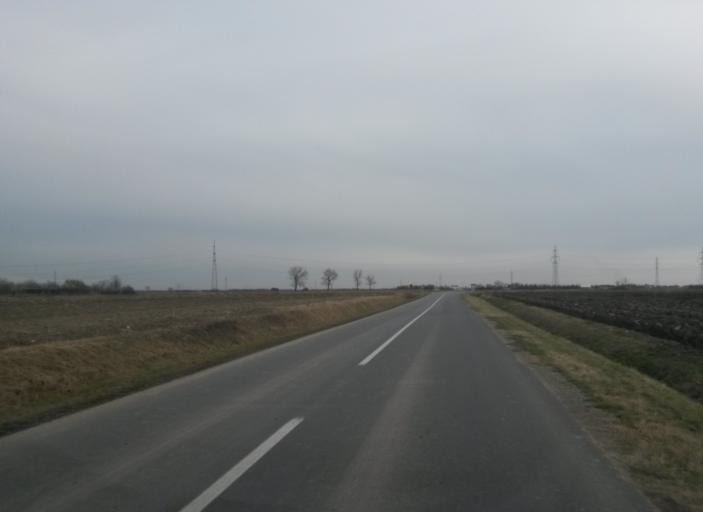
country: HR
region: Osjecko-Baranjska
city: Ovcara
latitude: 45.4976
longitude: 18.6146
